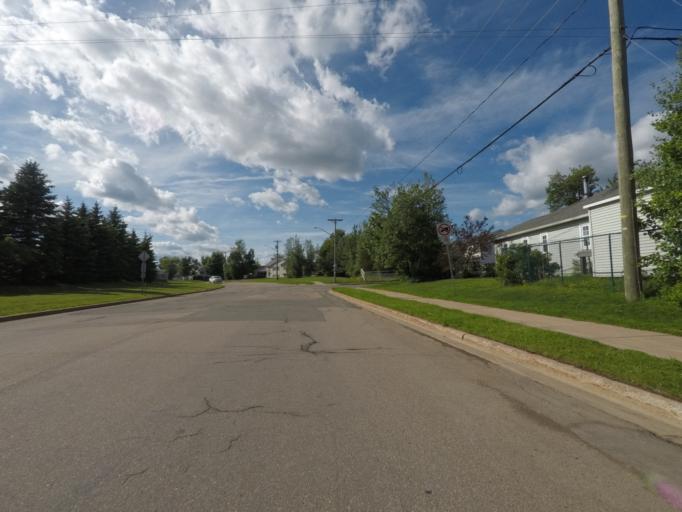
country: CA
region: New Brunswick
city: Moncton
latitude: 46.0974
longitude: -64.8336
